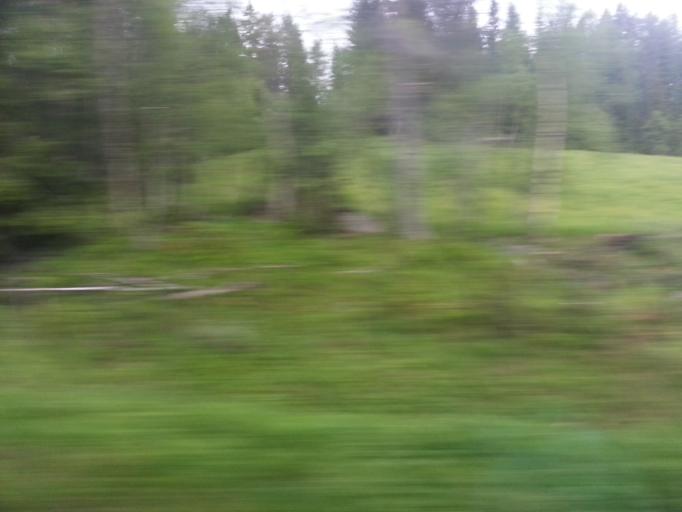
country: NO
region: Sor-Trondelag
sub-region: Rennebu
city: Berkak
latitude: 62.8696
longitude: 10.0379
